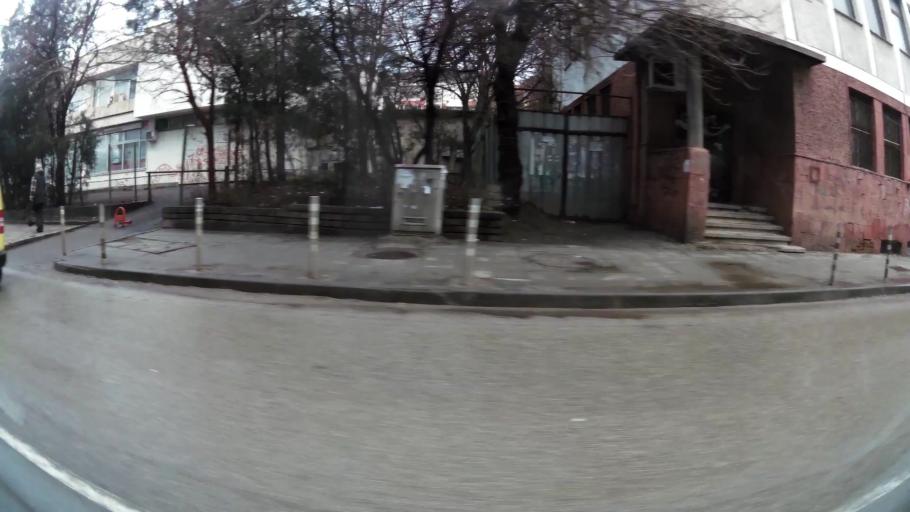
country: BG
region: Sofia-Capital
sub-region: Stolichna Obshtina
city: Sofia
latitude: 42.7244
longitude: 23.3062
